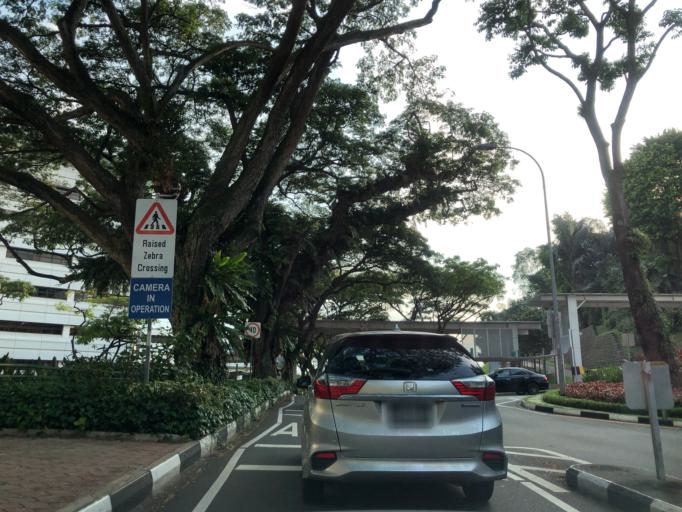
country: SG
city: Singapore
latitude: 1.2802
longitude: 103.8341
